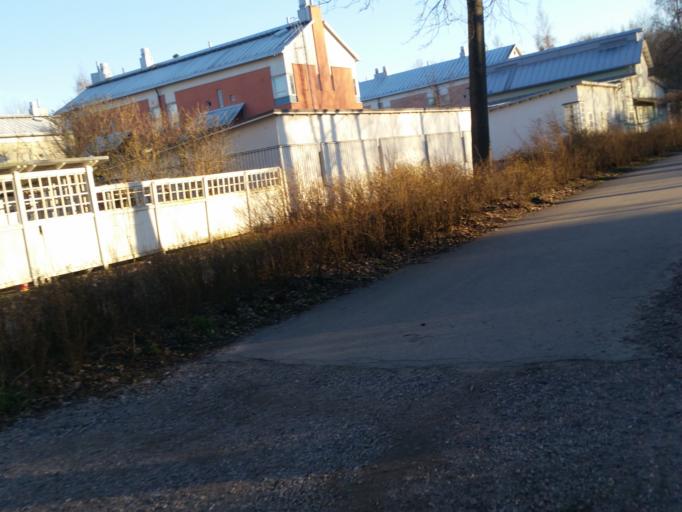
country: FI
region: Uusimaa
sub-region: Helsinki
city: Helsinki
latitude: 60.2089
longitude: 24.9653
